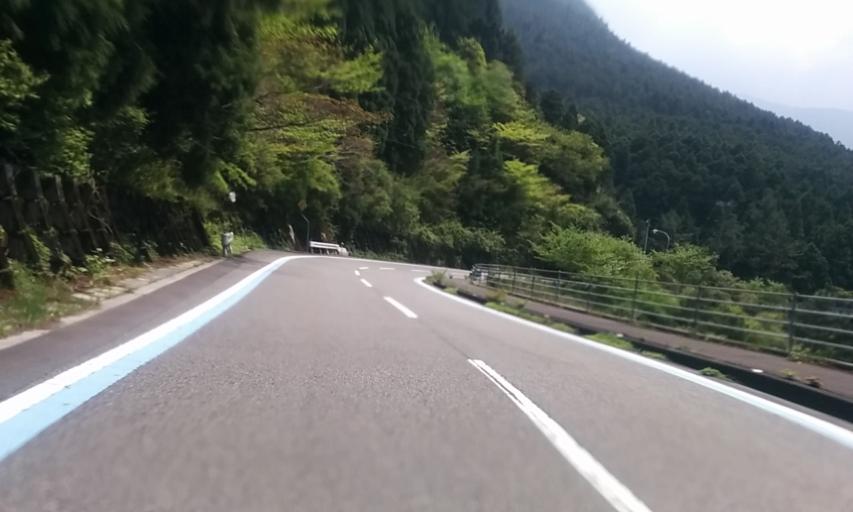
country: JP
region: Ehime
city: Saijo
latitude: 33.8219
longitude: 133.2342
